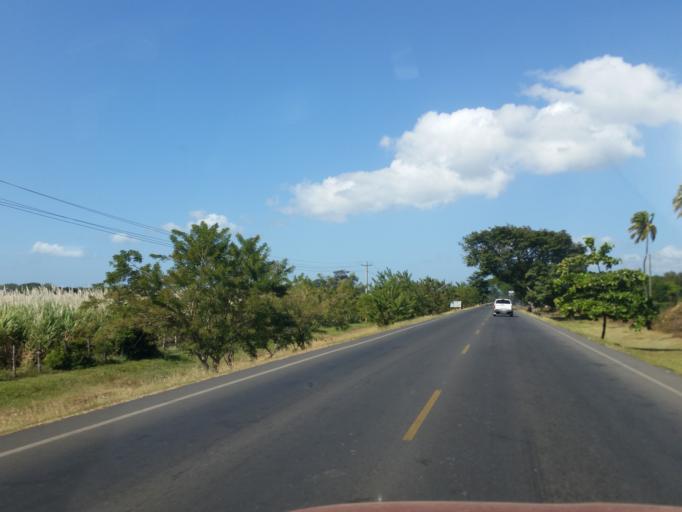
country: NI
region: Granada
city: Nandaime
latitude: 11.7504
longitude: -86.0342
